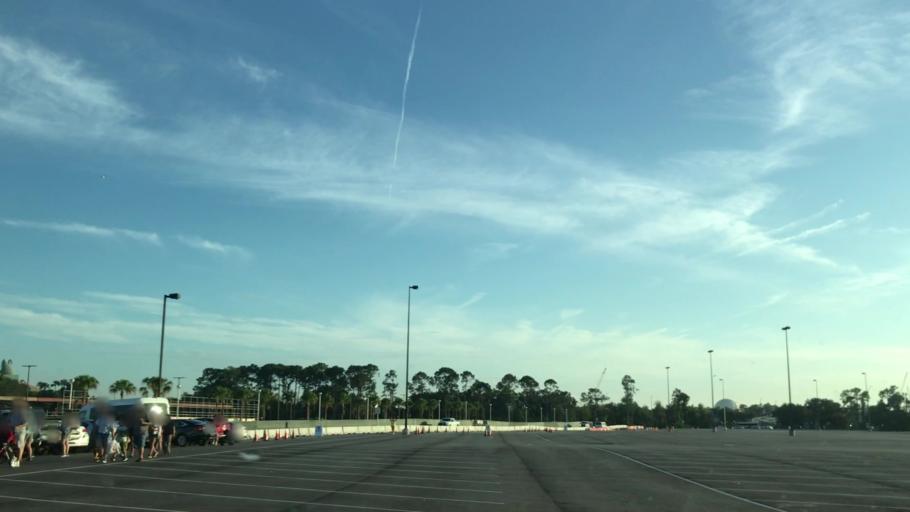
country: US
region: Florida
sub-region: Osceola County
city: Celebration
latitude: 28.3589
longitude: -81.5542
